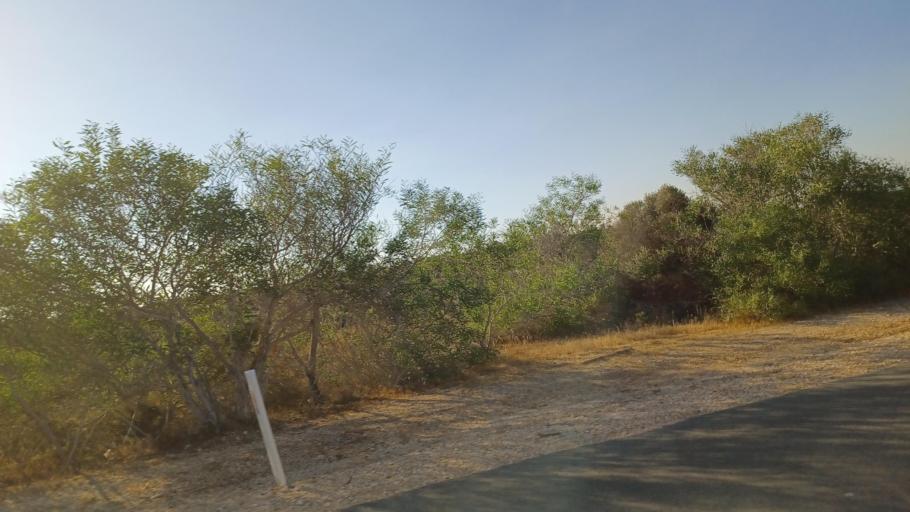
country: CY
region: Larnaka
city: Xylotymbou
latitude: 34.9938
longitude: 33.7424
